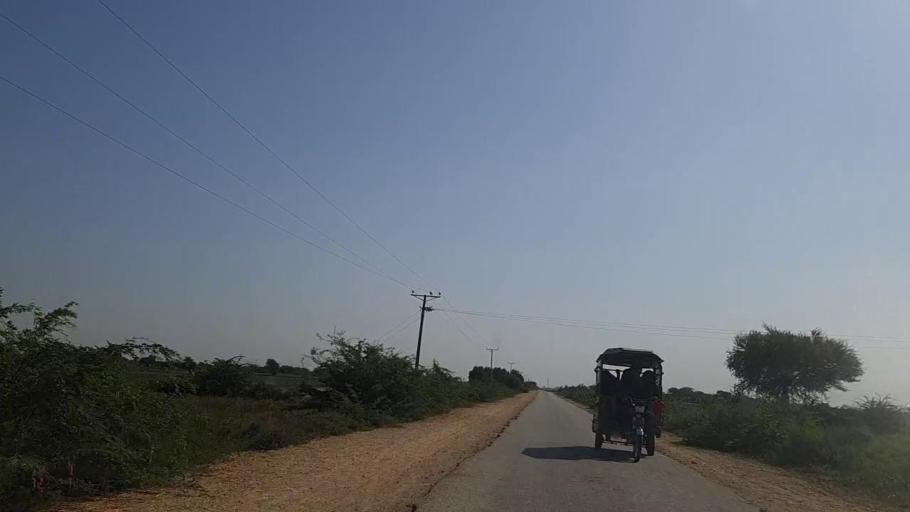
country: PK
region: Sindh
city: Mirpur Batoro
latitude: 24.6366
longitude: 68.2918
